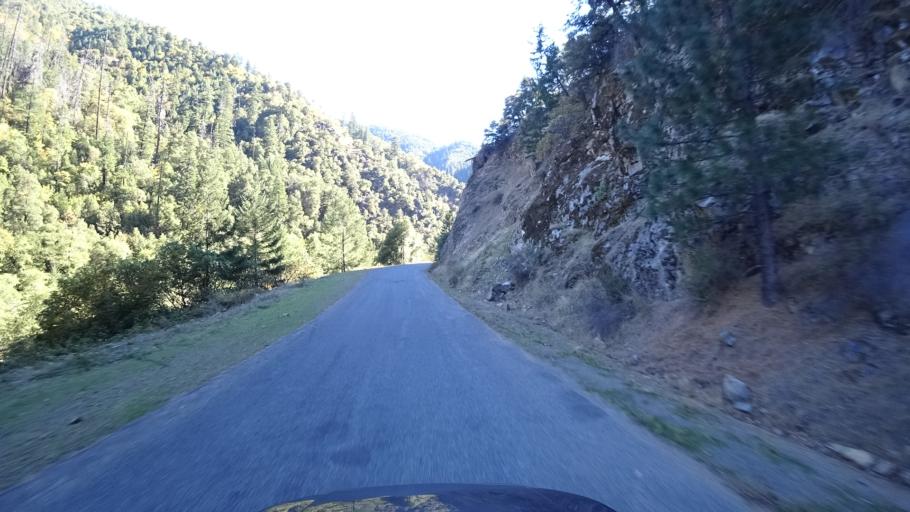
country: US
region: California
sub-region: Humboldt County
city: Willow Creek
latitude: 41.2846
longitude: -123.2555
